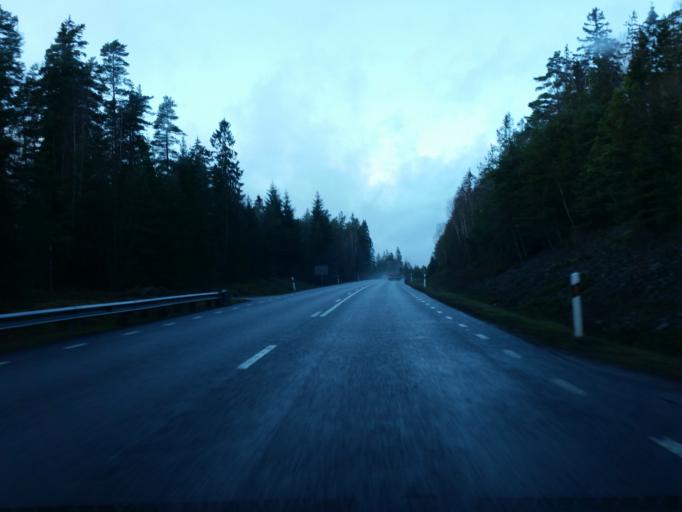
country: SE
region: Joenkoeping
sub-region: Gislaveds Kommun
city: Gislaved
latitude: 57.3292
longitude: 13.5297
